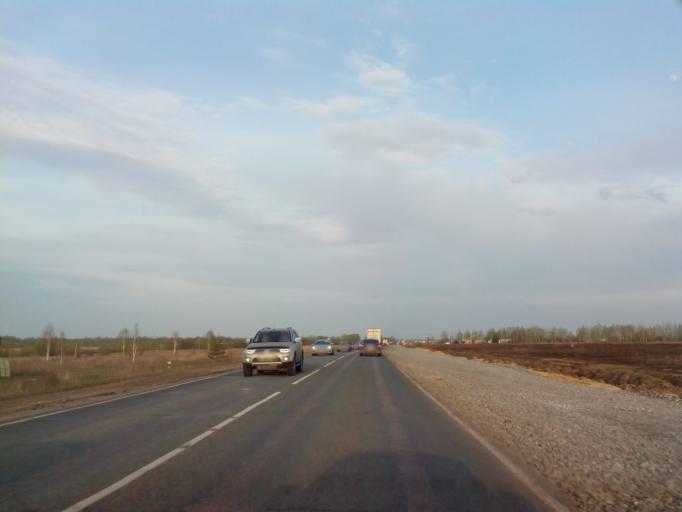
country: RU
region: Rjazan
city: Korablino
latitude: 53.7519
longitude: 39.8384
